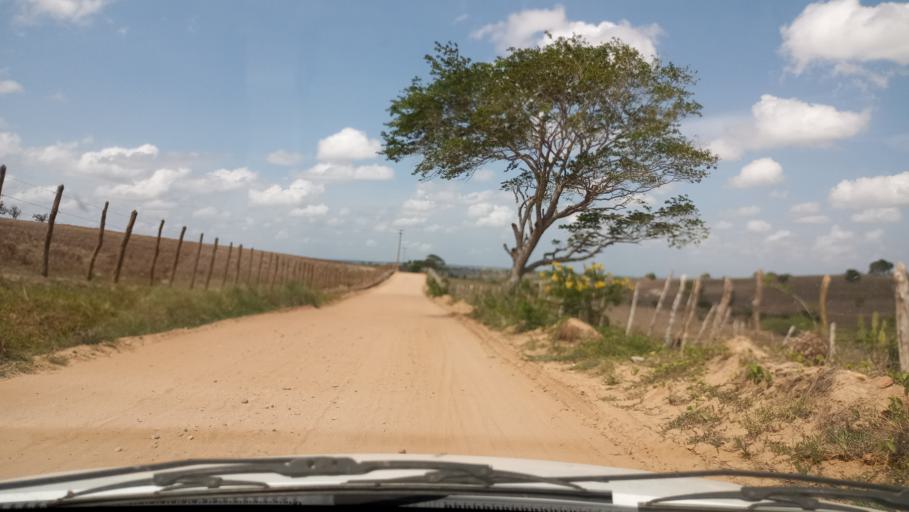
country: BR
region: Rio Grande do Norte
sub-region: Goianinha
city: Goianinha
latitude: -6.3451
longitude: -35.3287
